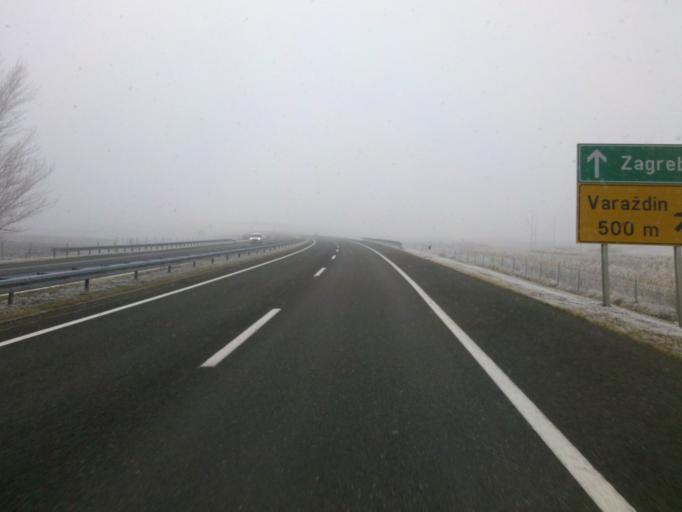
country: HR
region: Medimurska
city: Kursanec
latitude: 46.2672
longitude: 16.4082
